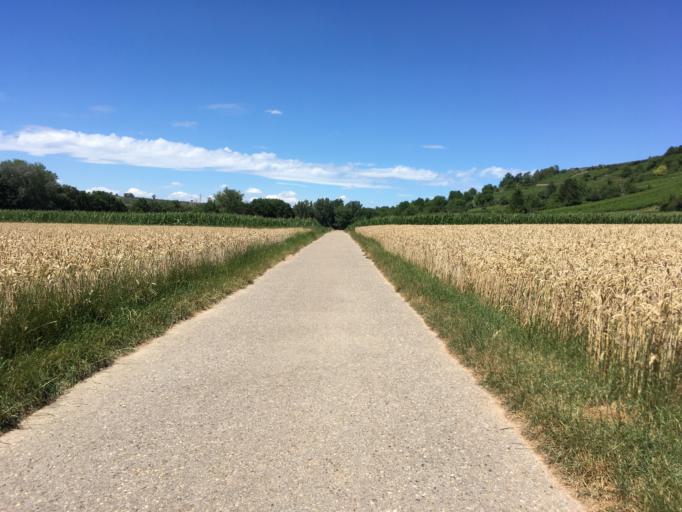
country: DE
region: Baden-Wuerttemberg
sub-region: Karlsruhe Region
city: Illingen
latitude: 48.9343
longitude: 8.9052
